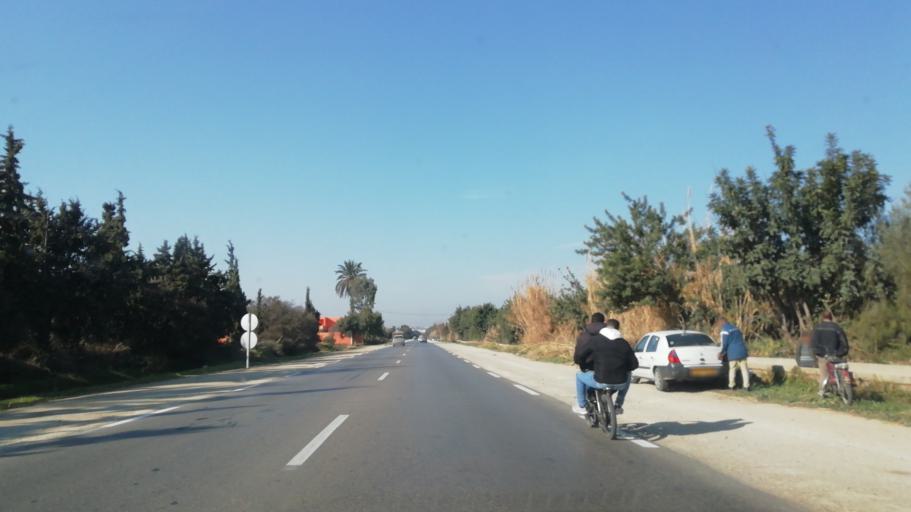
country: DZ
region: Relizane
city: Relizane
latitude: 35.7223
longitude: 0.5012
